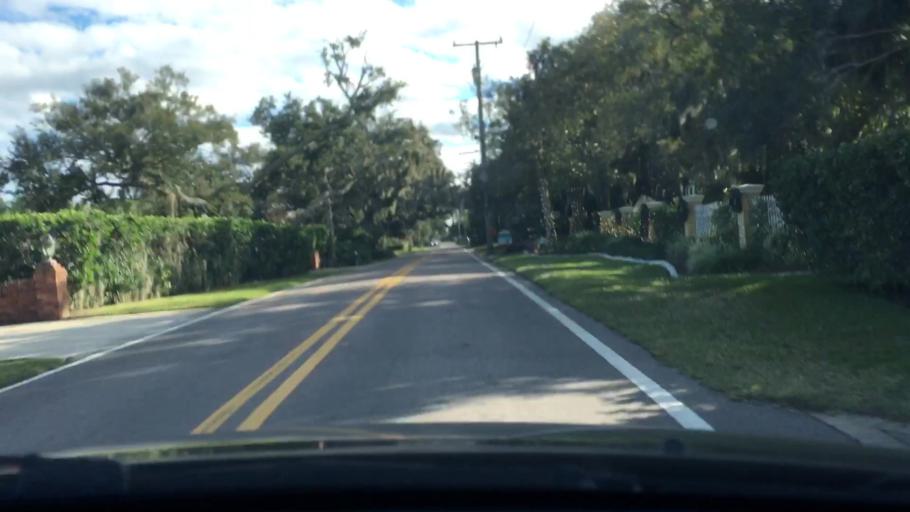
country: US
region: Florida
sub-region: Volusia County
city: Ormond Beach
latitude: 29.3139
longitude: -81.0590
